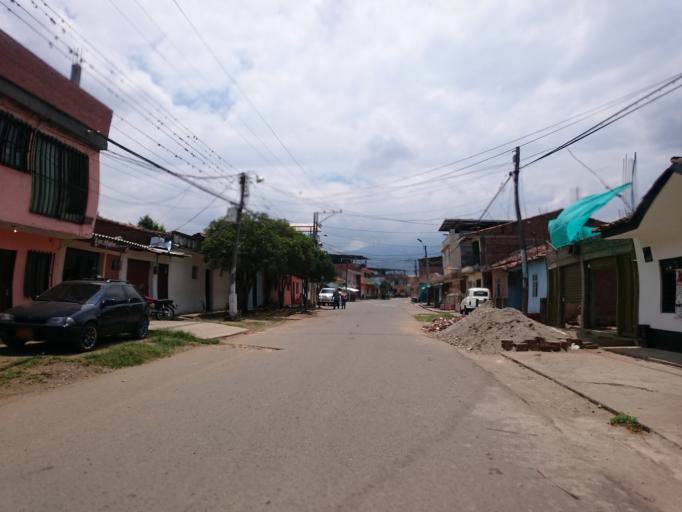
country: CO
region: Cauca
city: Santander de Quilichao
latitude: 3.0105
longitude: -76.4883
